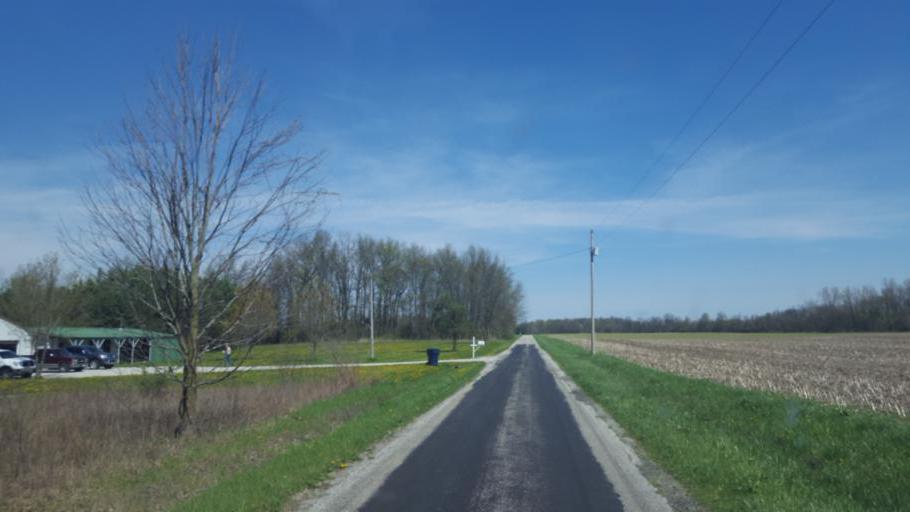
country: US
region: Ohio
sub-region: Morrow County
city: Mount Gilead
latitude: 40.6069
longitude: -82.8853
